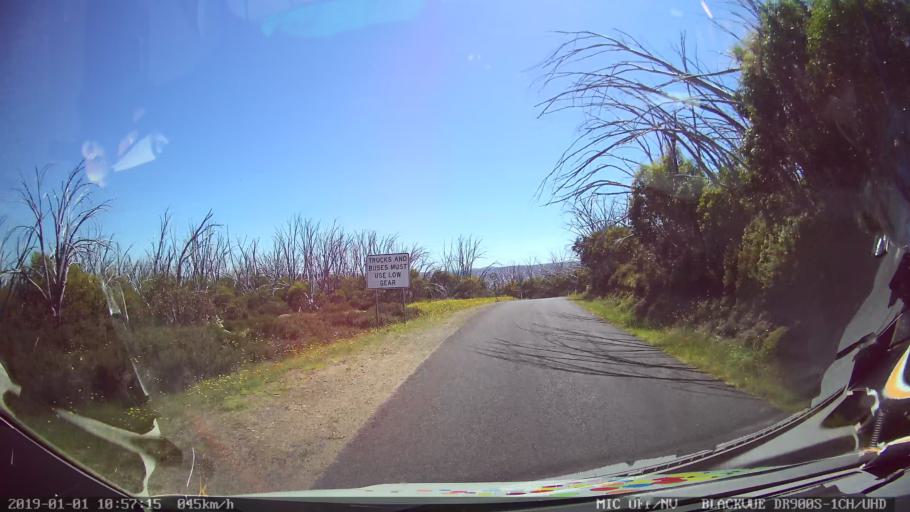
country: AU
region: New South Wales
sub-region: Snowy River
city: Jindabyne
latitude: -35.9987
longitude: 148.3957
